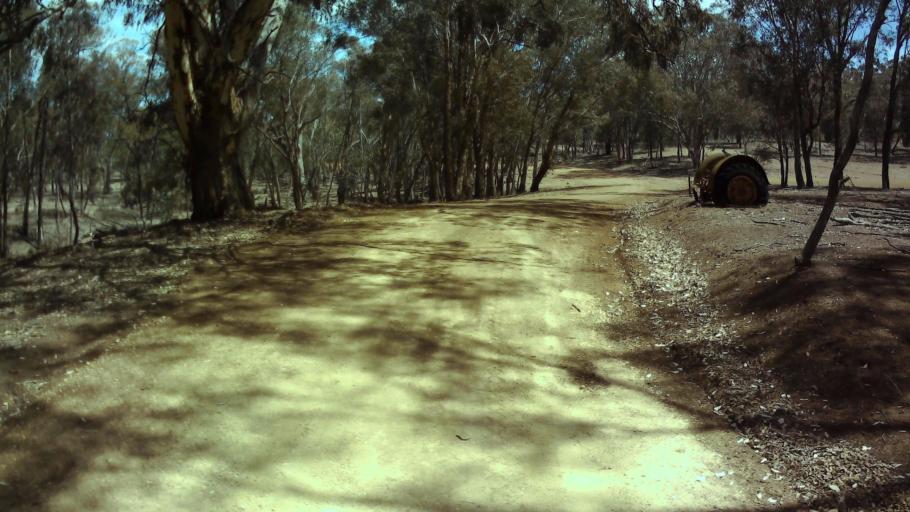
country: AU
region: New South Wales
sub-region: Weddin
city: Grenfell
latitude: -33.7988
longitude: 148.1602
